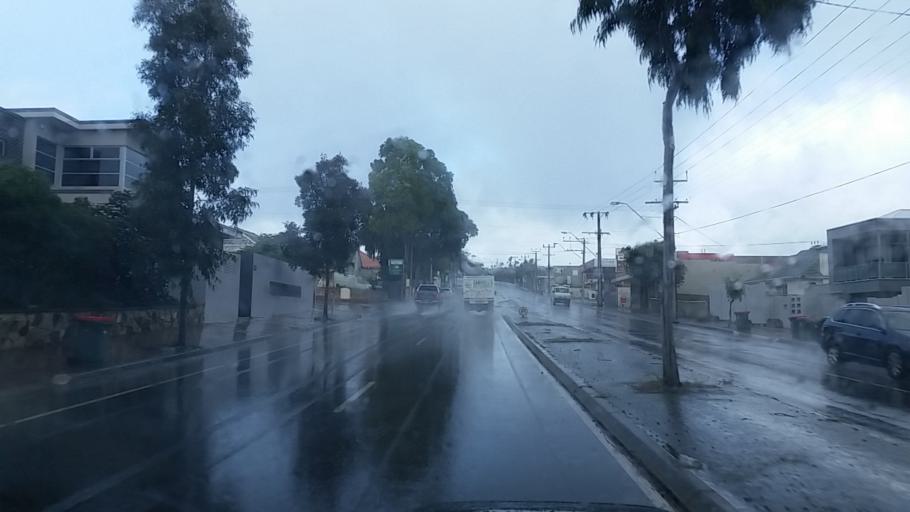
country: AU
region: South Australia
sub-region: Adelaide Hills
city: Seacliff
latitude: -35.0350
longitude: 138.5244
